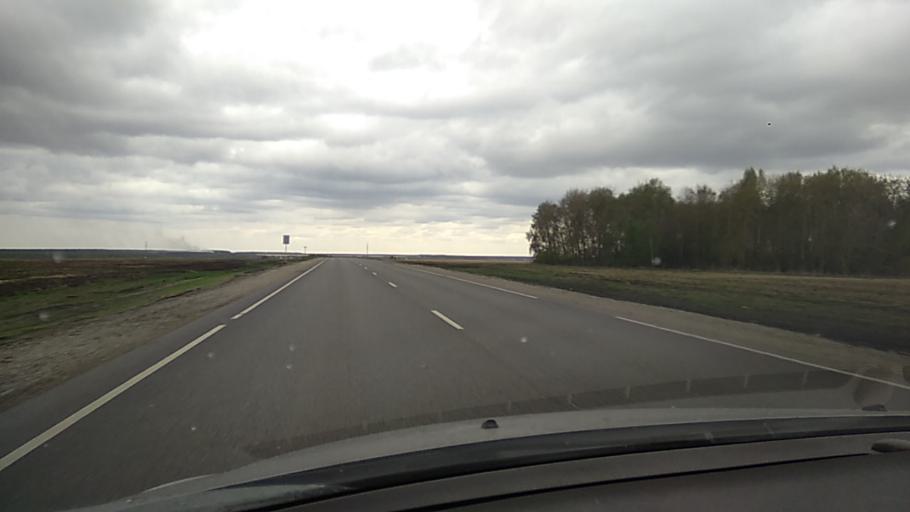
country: RU
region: Kurgan
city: Kataysk
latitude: 56.3111
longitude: 62.6034
